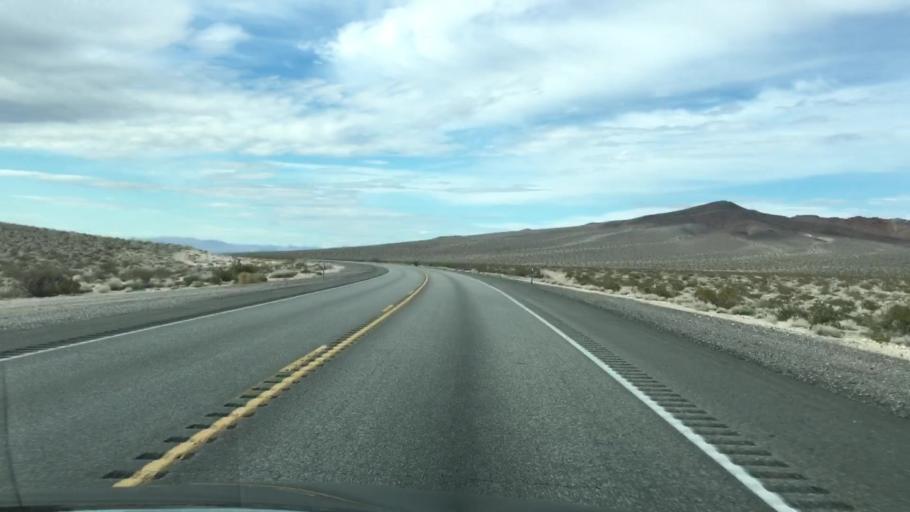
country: US
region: Nevada
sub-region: Nye County
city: Beatty
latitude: 36.6306
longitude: -116.3174
